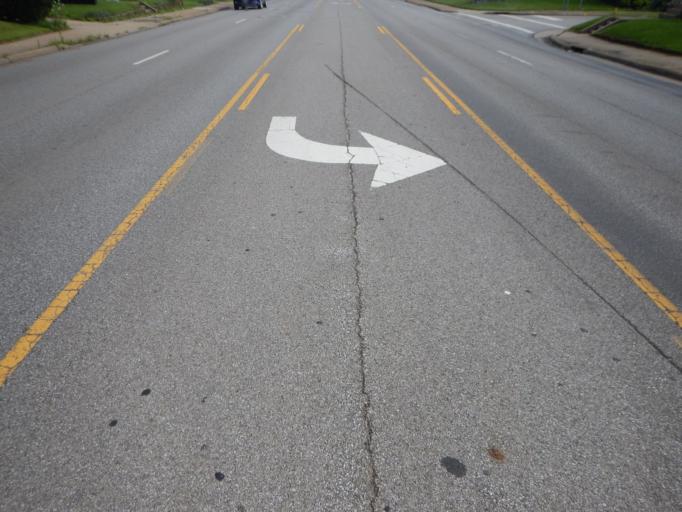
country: US
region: Ohio
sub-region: Muskingum County
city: North Zanesville
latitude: 39.9629
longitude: -82.0102
